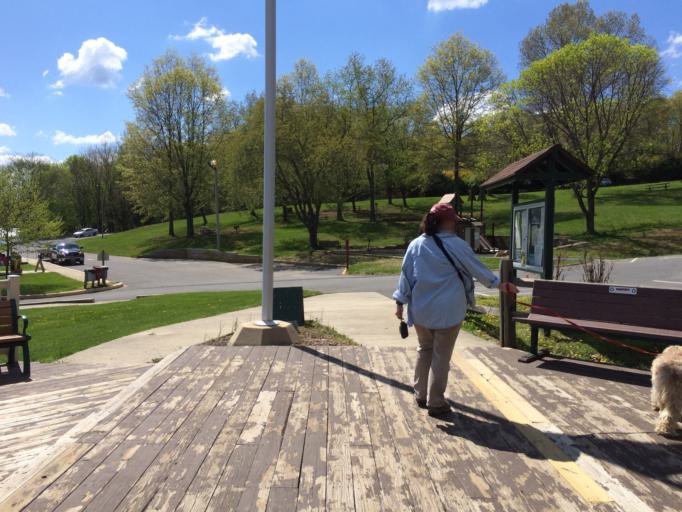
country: US
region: Maryland
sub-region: Carroll County
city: Sykesville
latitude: 39.3985
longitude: -76.9863
